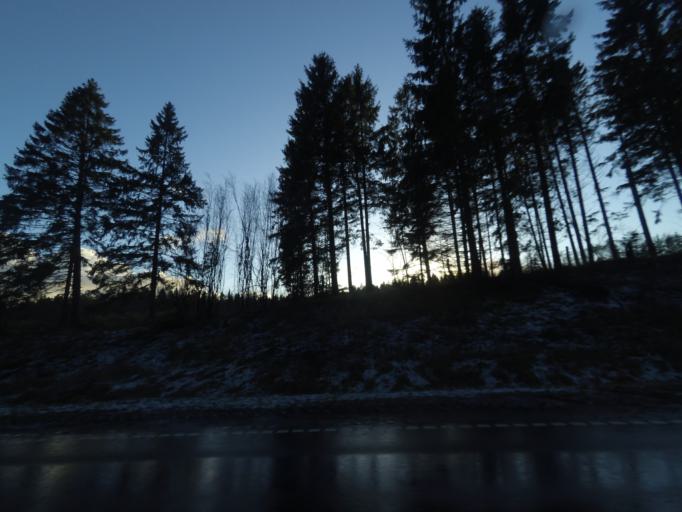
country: DK
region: Central Jutland
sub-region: Ikast-Brande Kommune
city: Brande
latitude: 56.0022
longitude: 9.1760
